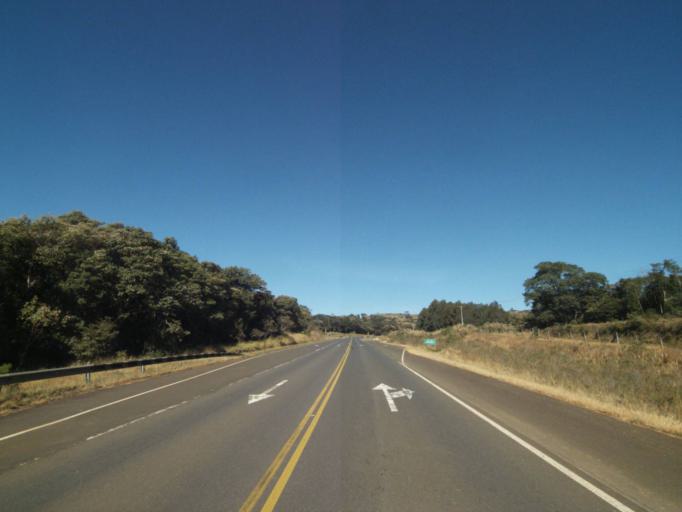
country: BR
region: Parana
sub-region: Tibagi
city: Tibagi
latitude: -24.4034
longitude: -50.3426
